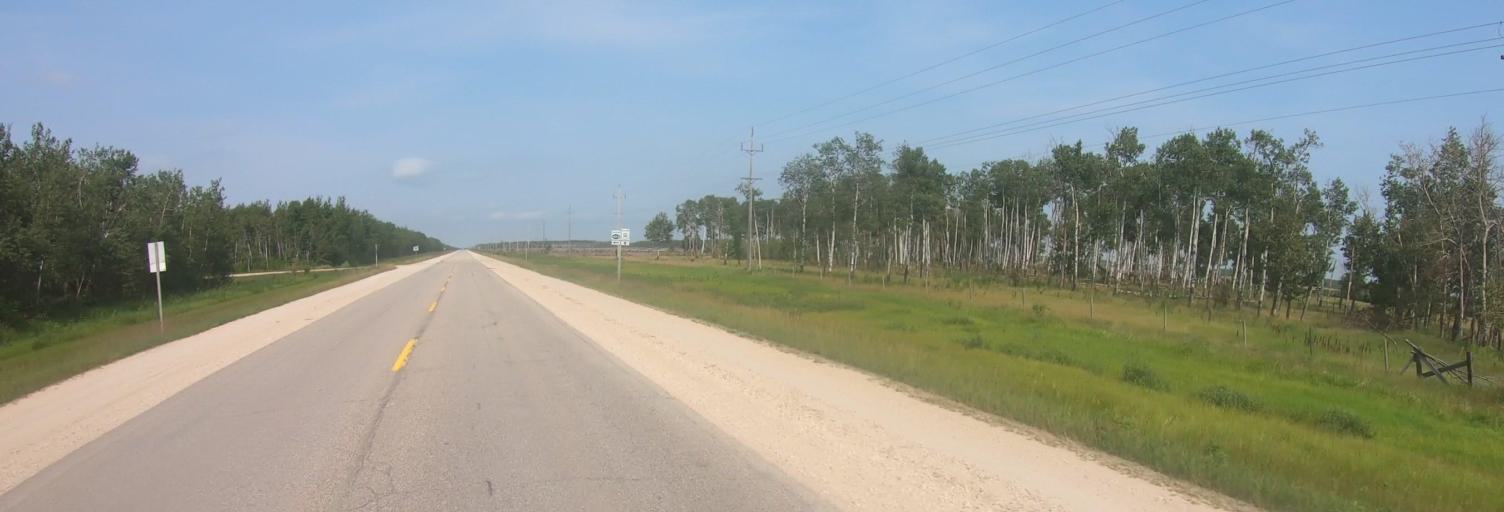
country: CA
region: Manitoba
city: La Broquerie
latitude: 49.3267
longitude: -96.6004
